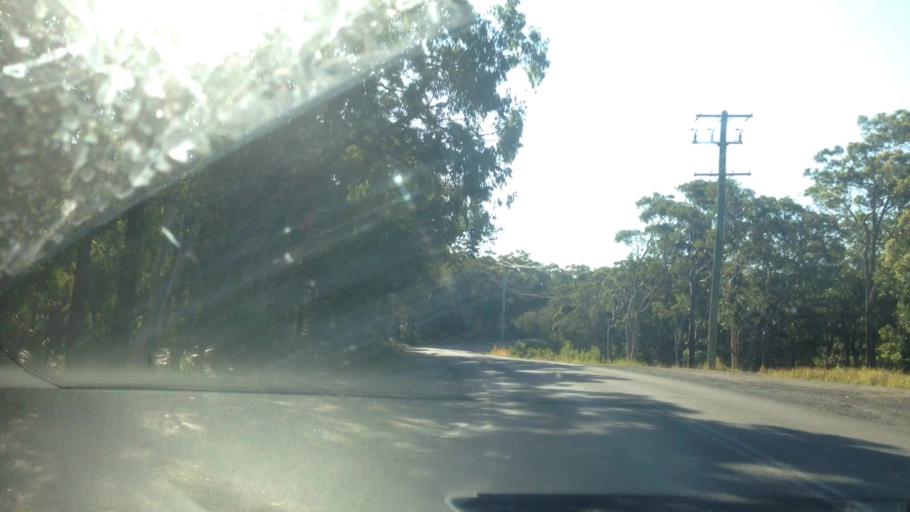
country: AU
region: New South Wales
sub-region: Lake Macquarie Shire
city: Arcadia vale
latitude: -33.1106
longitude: 151.5605
